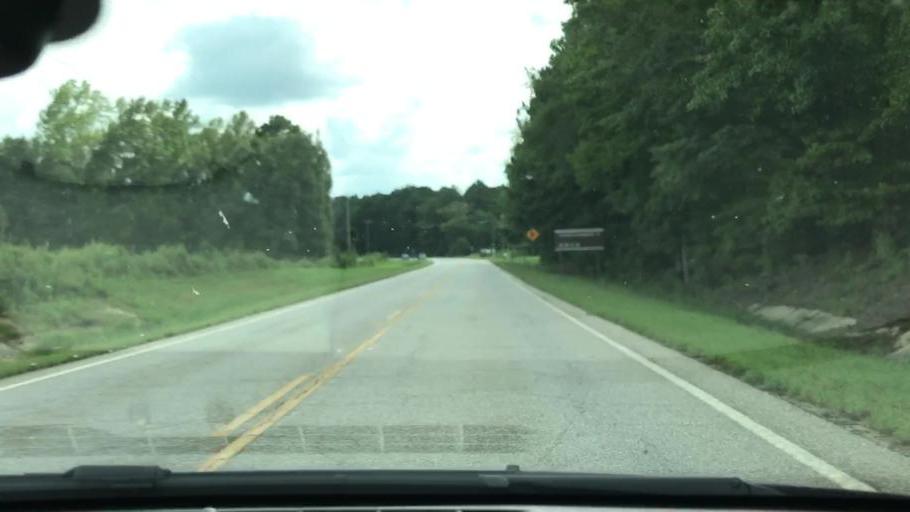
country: US
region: Georgia
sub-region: Clay County
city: Fort Gaines
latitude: 31.6951
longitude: -85.0453
